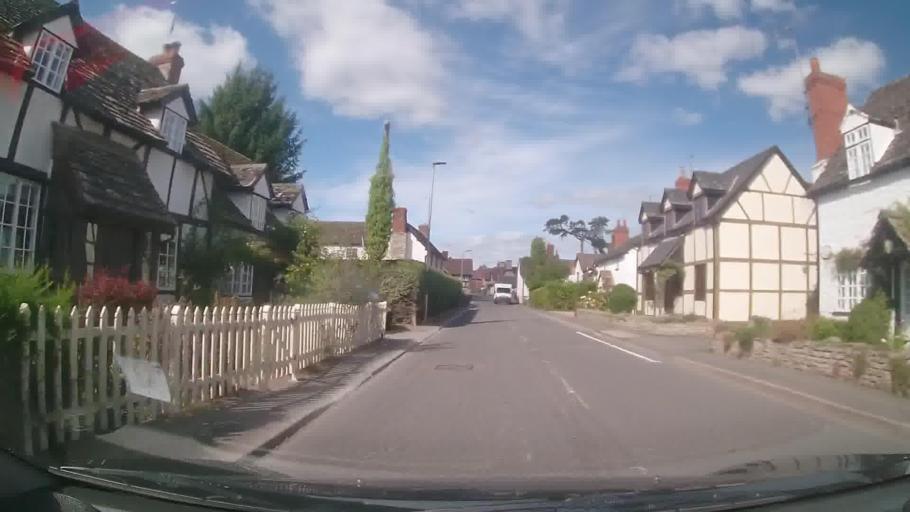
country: GB
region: England
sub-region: Herefordshire
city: Kinnersley
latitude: 52.1383
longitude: -3.0068
